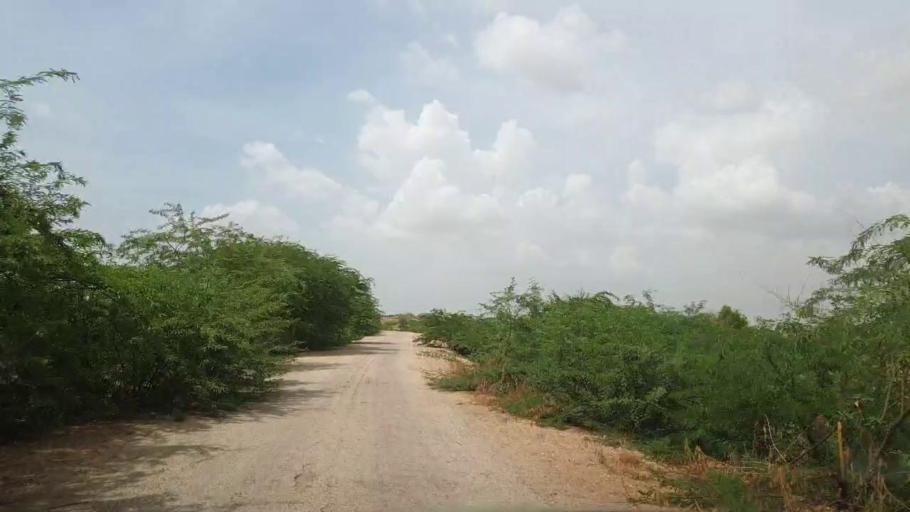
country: PK
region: Sindh
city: Kot Diji
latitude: 27.2473
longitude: 69.0780
